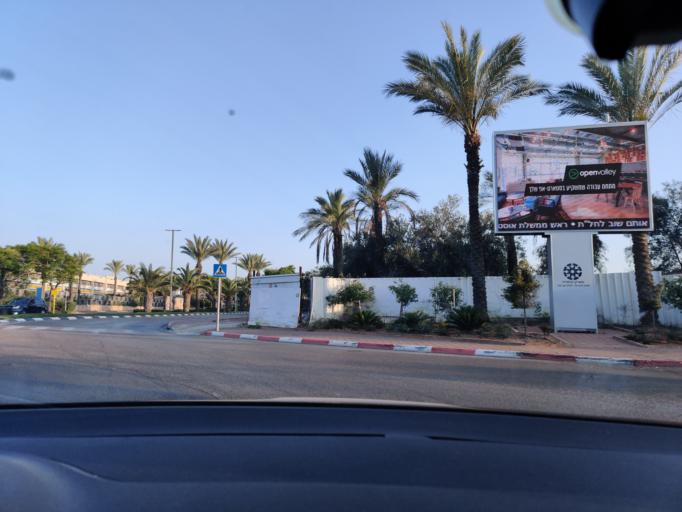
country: IL
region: Haifa
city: Qesarya
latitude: 32.4815
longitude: 34.9480
